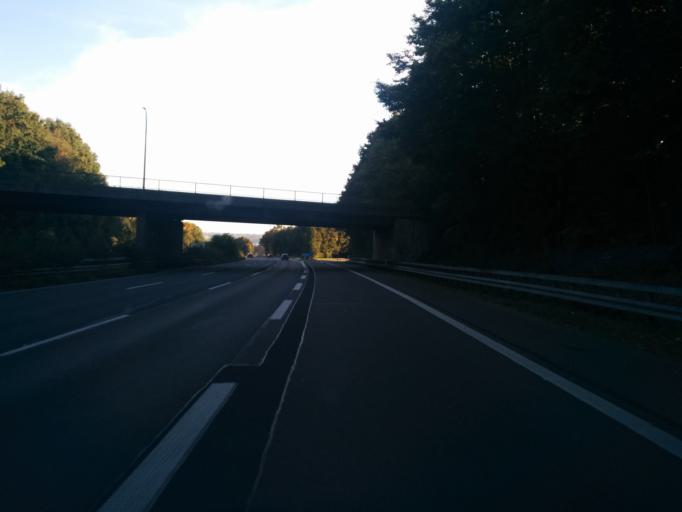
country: DE
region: North Rhine-Westphalia
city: Witten
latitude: 51.4804
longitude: 7.3916
